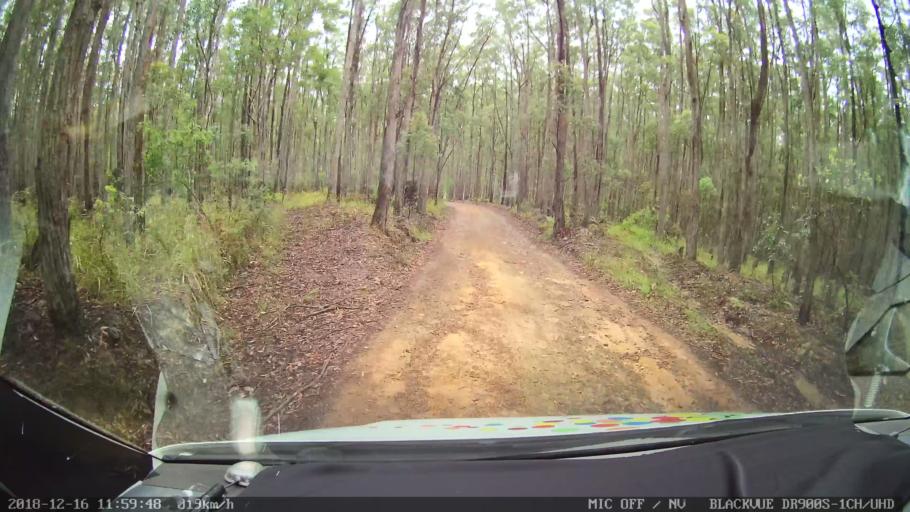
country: AU
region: New South Wales
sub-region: Tenterfield Municipality
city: Carrolls Creek
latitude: -28.9268
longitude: 152.3148
